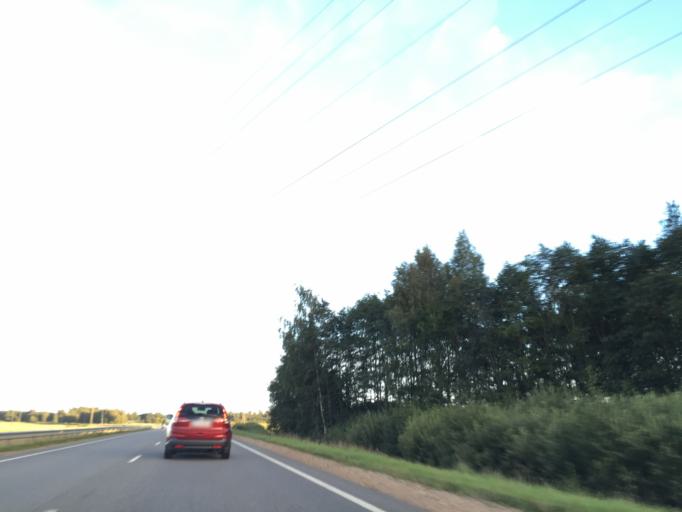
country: LV
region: Broceni
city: Broceni
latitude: 56.6658
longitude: 22.5962
